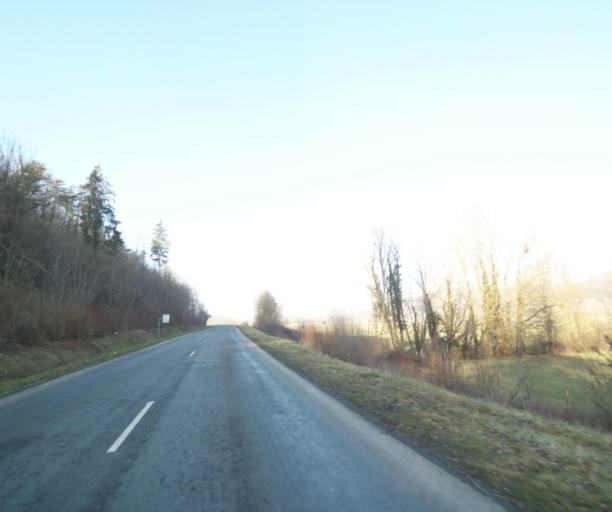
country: FR
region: Champagne-Ardenne
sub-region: Departement de la Haute-Marne
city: Chevillon
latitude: 48.4988
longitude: 5.1196
